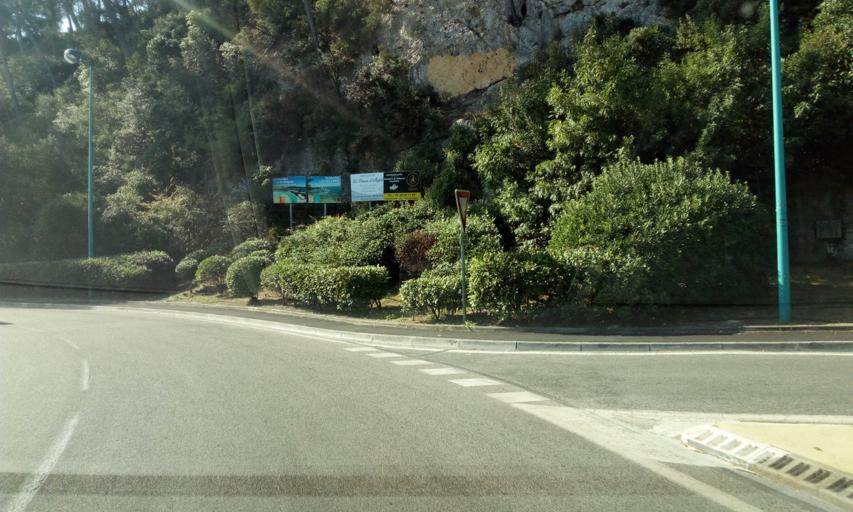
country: FR
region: Provence-Alpes-Cote d'Azur
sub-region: Departement du Var
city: Bandol
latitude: 43.1424
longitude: 5.7680
